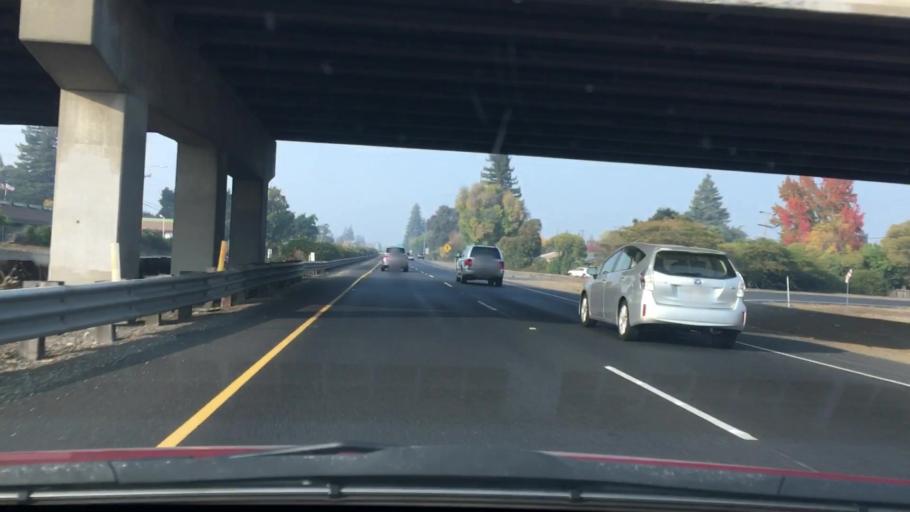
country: US
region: California
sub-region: Napa County
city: Napa
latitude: 38.3068
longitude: -122.3047
